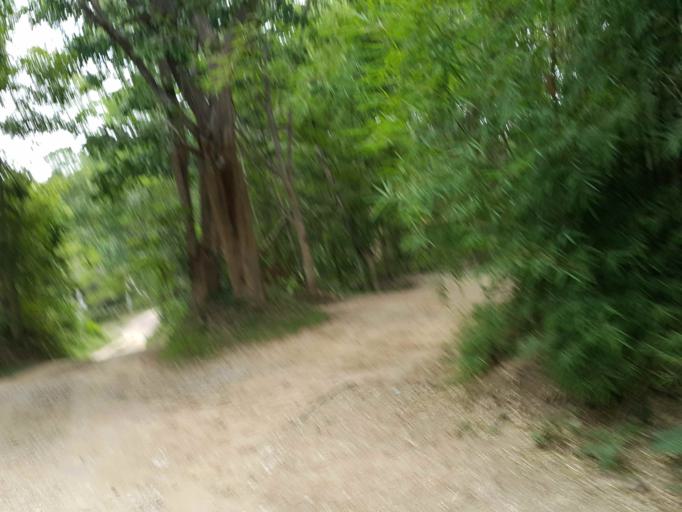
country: TH
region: Chiang Mai
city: Hang Dong
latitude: 18.7626
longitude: 98.9041
